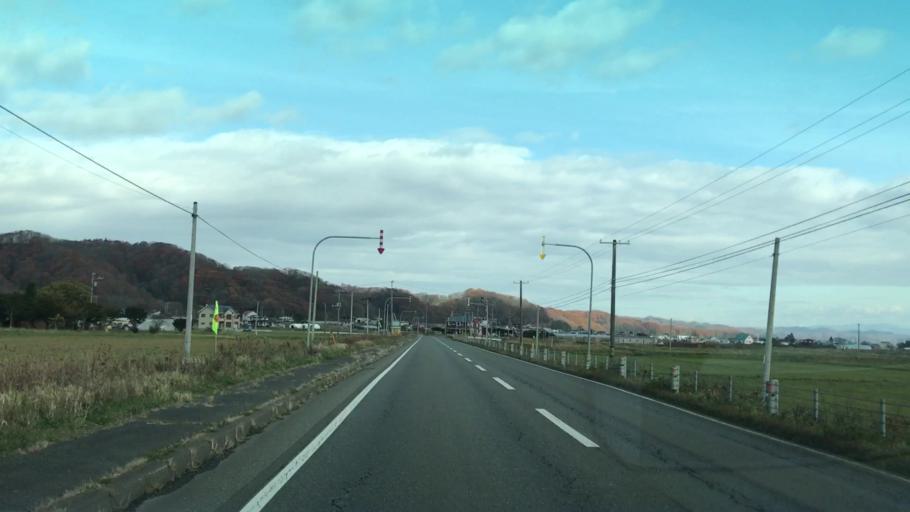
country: JP
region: Hokkaido
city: Shizunai-furukawacho
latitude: 42.5413
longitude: 142.0569
